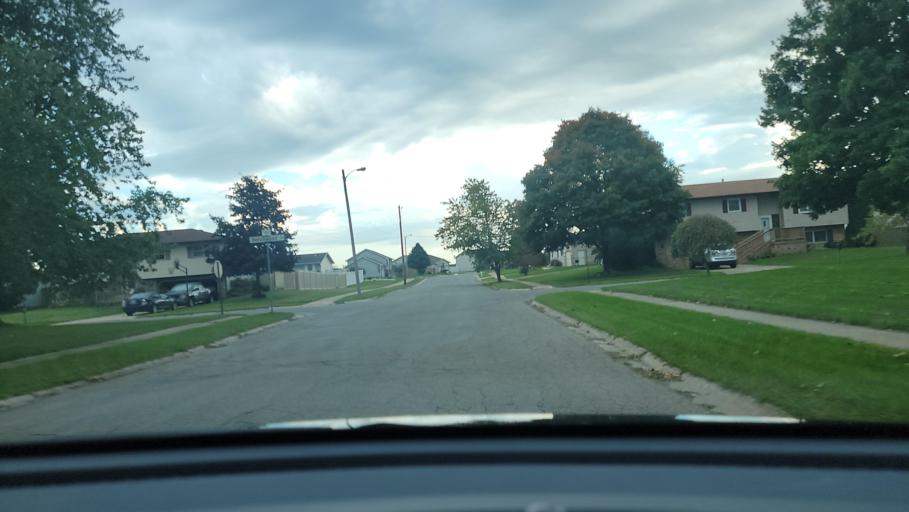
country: US
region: Indiana
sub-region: Porter County
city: Portage
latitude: 41.5690
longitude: -87.1602
